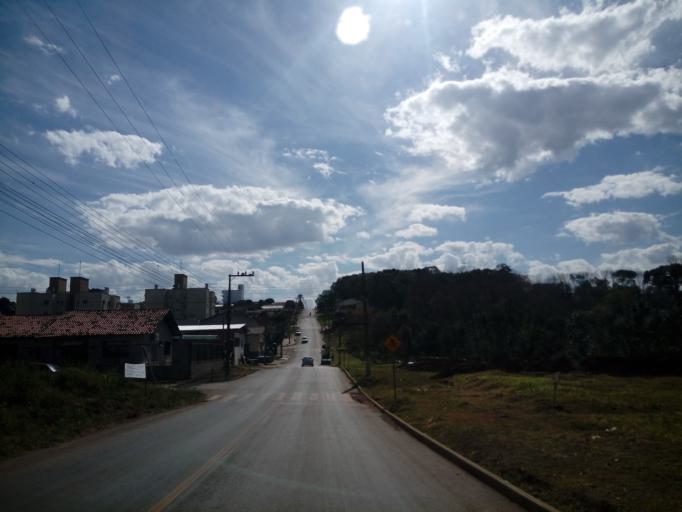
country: BR
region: Santa Catarina
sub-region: Chapeco
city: Chapeco
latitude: -27.1043
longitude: -52.6703
